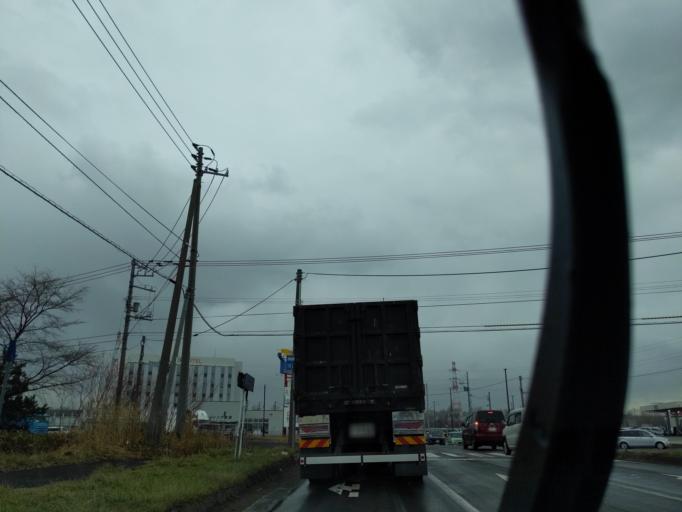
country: JP
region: Hokkaido
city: Ishikari
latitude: 43.1857
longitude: 141.3095
